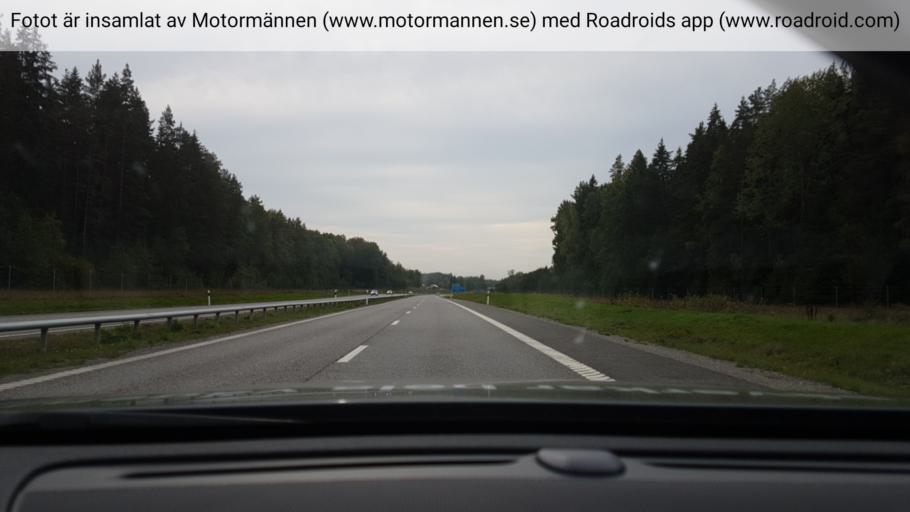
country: SE
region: Stockholm
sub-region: Nynashamns Kommun
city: Osmo
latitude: 59.0067
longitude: 17.9413
